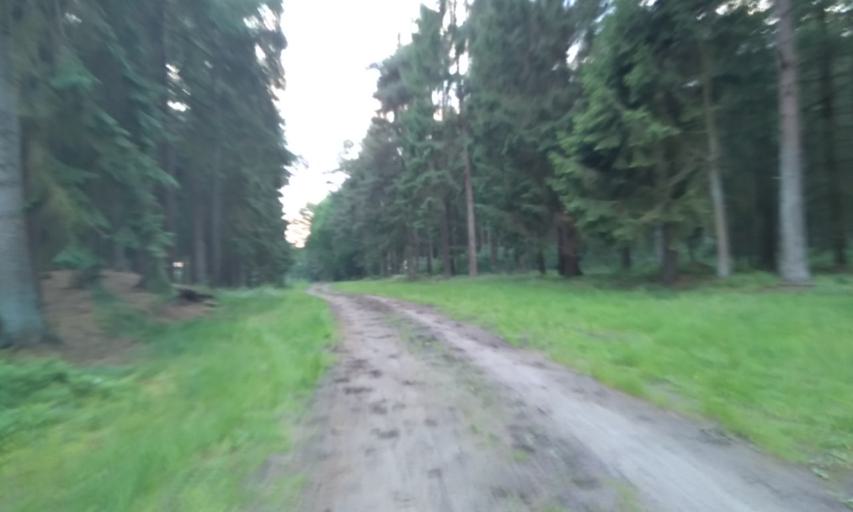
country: DE
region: Lower Saxony
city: Agathenburg
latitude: 53.5312
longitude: 9.5033
